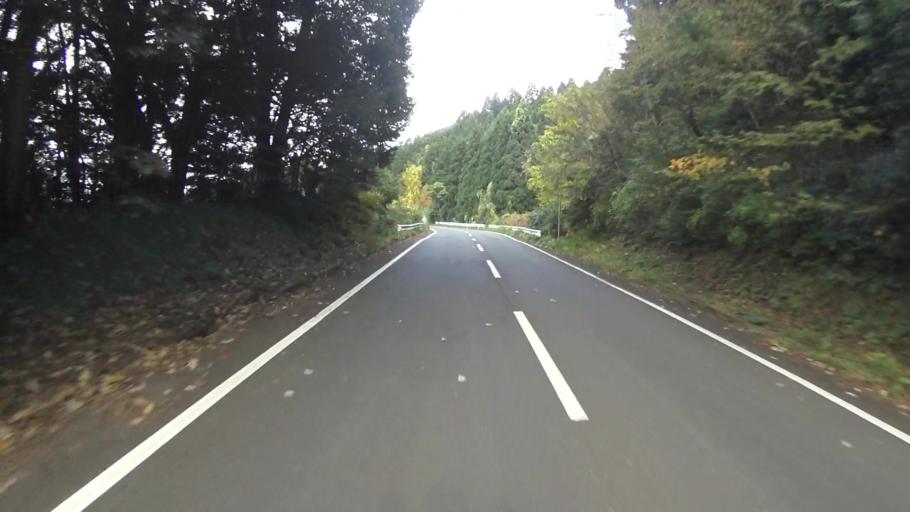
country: JP
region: Kyoto
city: Maizuru
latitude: 35.5627
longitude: 135.4558
